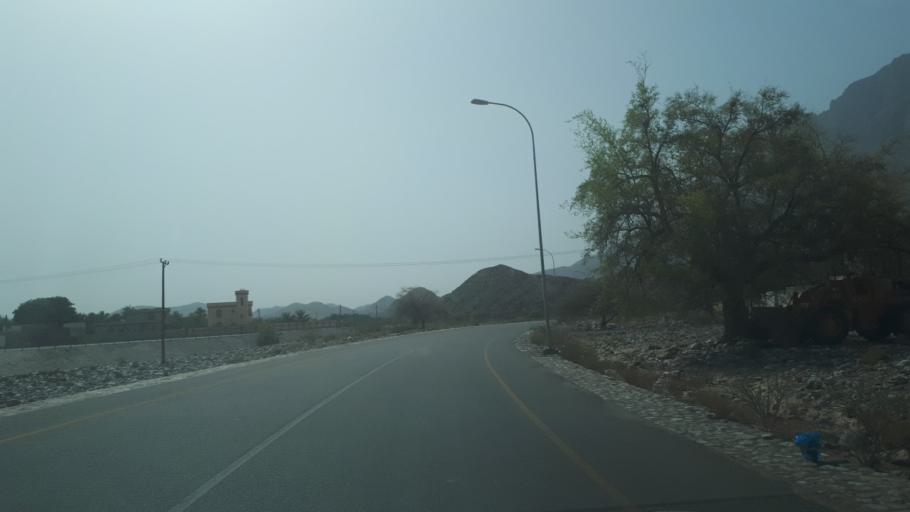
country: OM
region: Muhafazat ad Dakhiliyah
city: Bahla'
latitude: 23.2154
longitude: 57.0155
